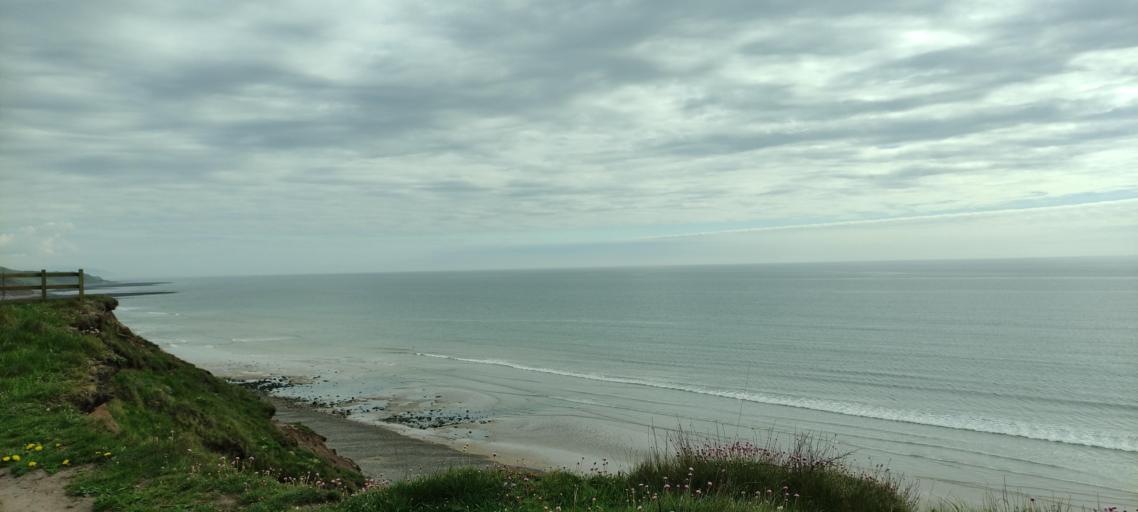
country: GB
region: England
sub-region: Cumbria
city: Saint Bees
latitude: 54.4886
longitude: -3.6019
